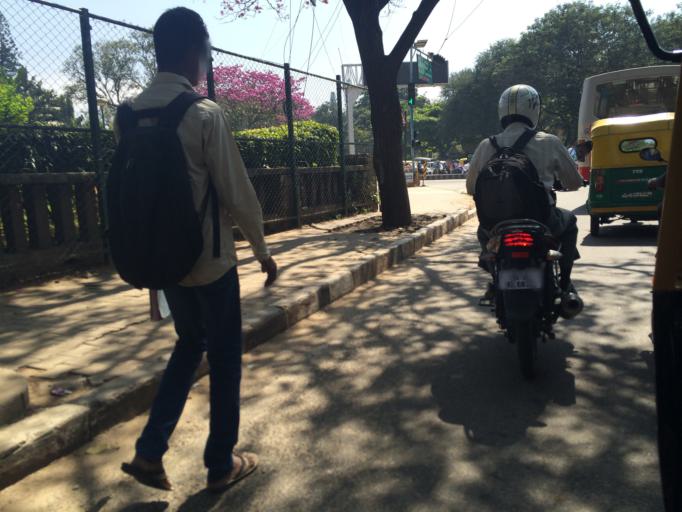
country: IN
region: Karnataka
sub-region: Bangalore Urban
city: Bangalore
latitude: 12.9771
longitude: 77.5992
